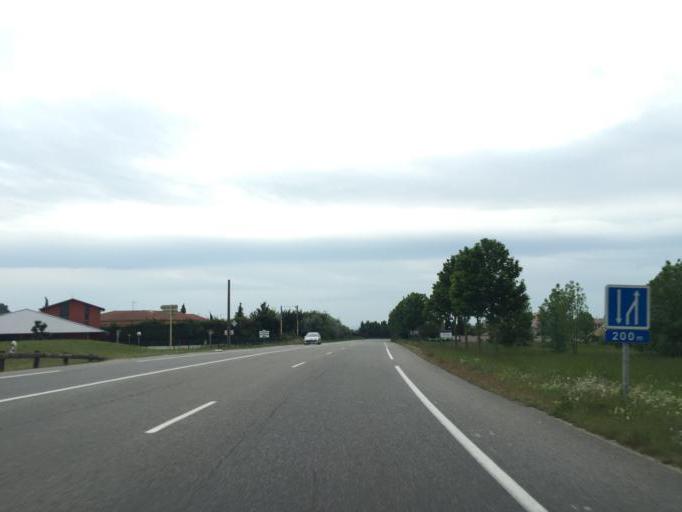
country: FR
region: Rhone-Alpes
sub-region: Departement de la Drome
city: Chabeuil
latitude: 44.9101
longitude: 5.0194
